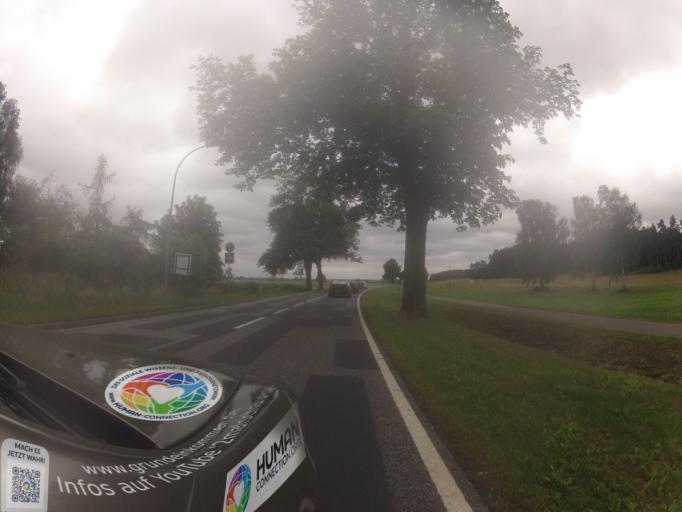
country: DE
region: Mecklenburg-Vorpommern
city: Jatznick
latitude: 53.5618
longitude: 13.9649
